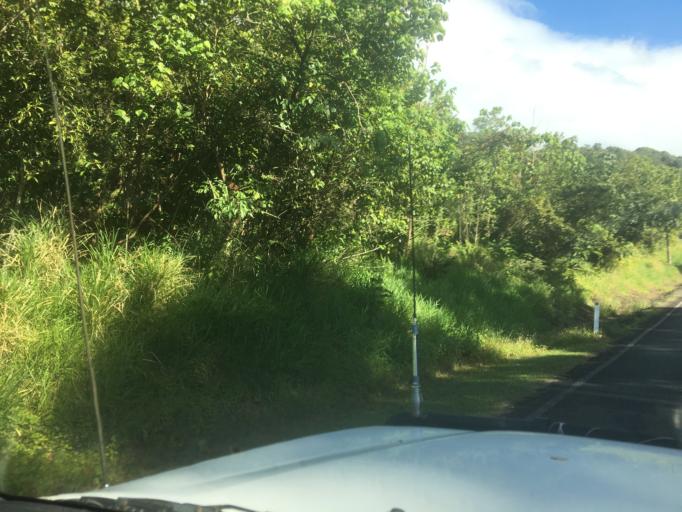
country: AU
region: Queensland
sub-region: Cassowary Coast
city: Innisfail
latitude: -17.3466
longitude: 145.8766
